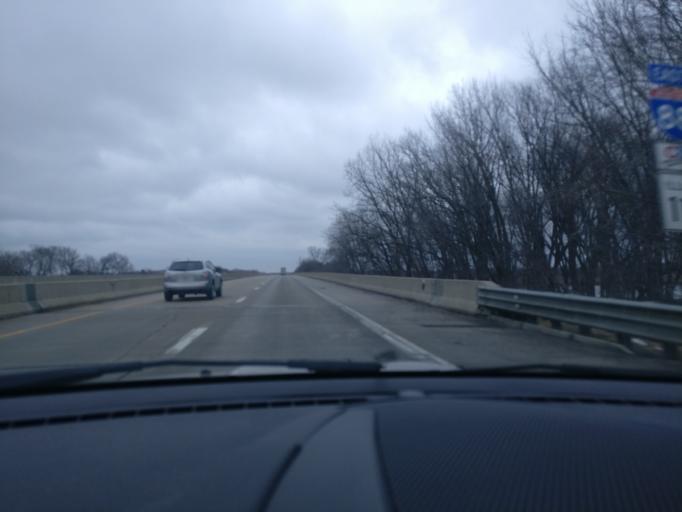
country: US
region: Illinois
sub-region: Whiteside County
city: Sterling
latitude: 41.7568
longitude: -89.7747
